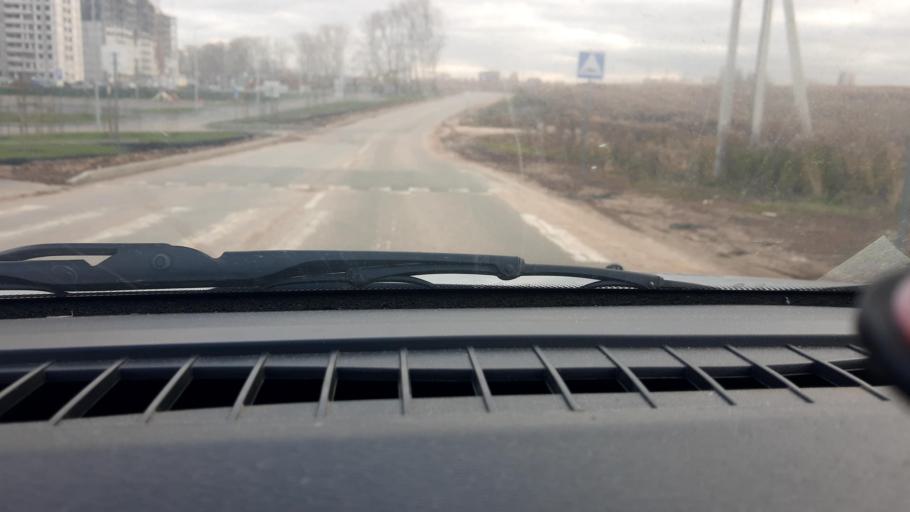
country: RU
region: Nizjnij Novgorod
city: Afonino
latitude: 56.2728
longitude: 44.0424
